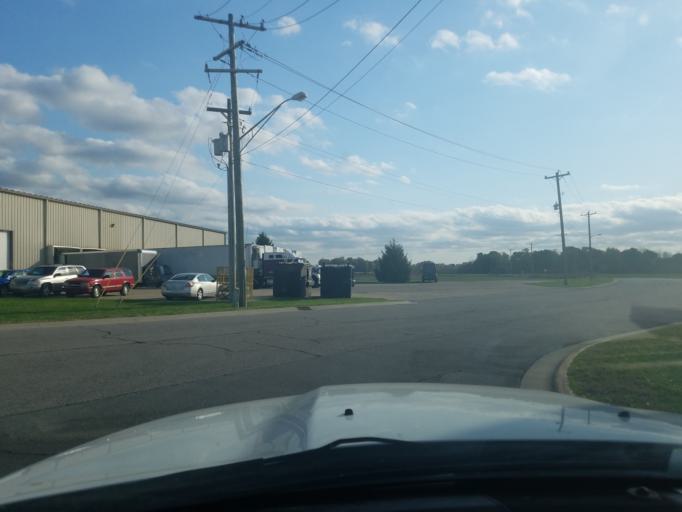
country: US
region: Indiana
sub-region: Jackson County
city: Seymour
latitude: 38.9694
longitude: -85.8577
